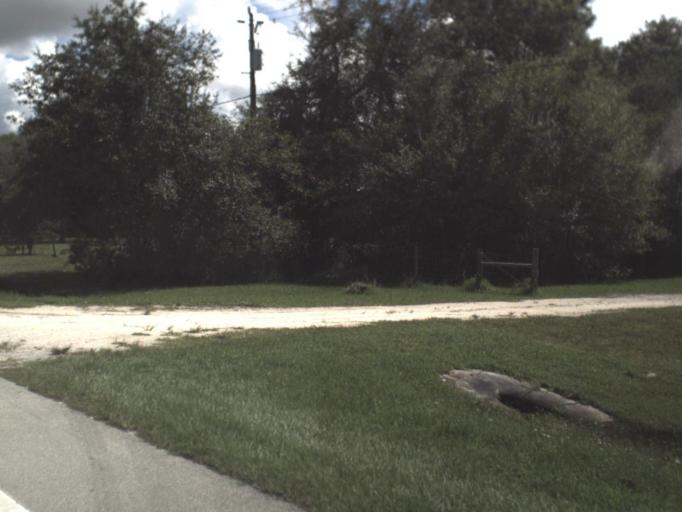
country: US
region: Florida
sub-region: DeSoto County
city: Arcadia
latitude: 27.2311
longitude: -81.9125
